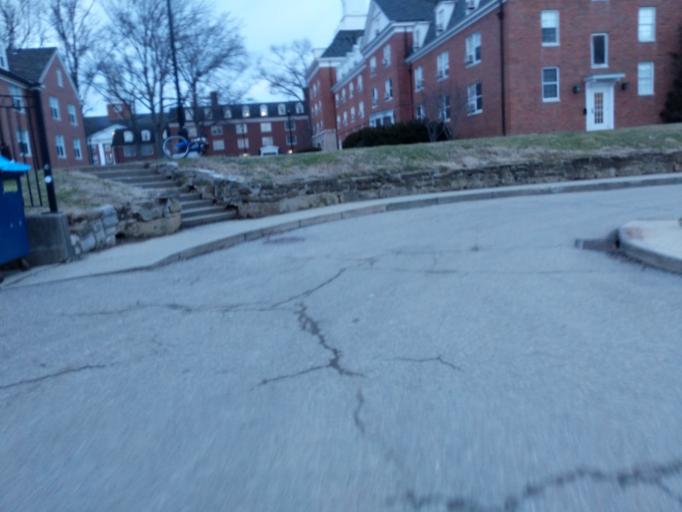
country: US
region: Ohio
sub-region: Athens County
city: Athens
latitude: 39.3257
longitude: -82.0961
